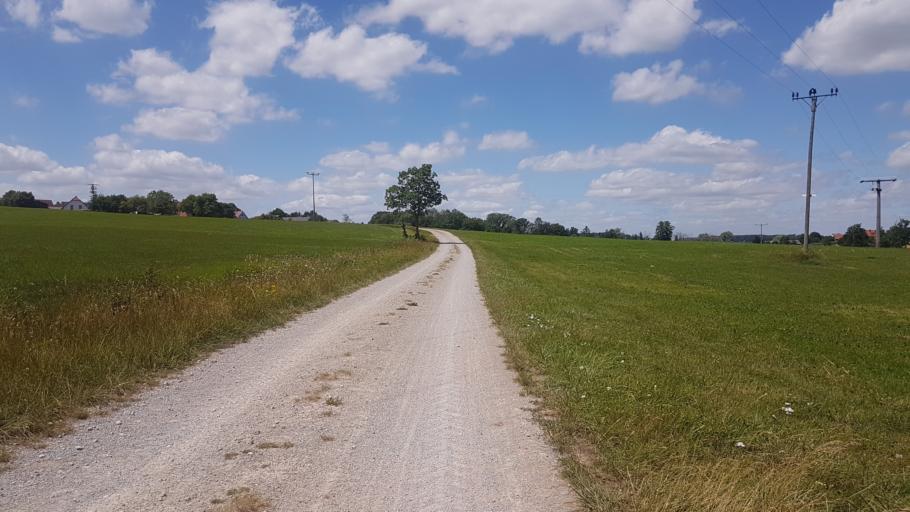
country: DE
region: Bavaria
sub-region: Regierungsbezirk Mittelfranken
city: Leutershausen
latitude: 49.3202
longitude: 10.3839
